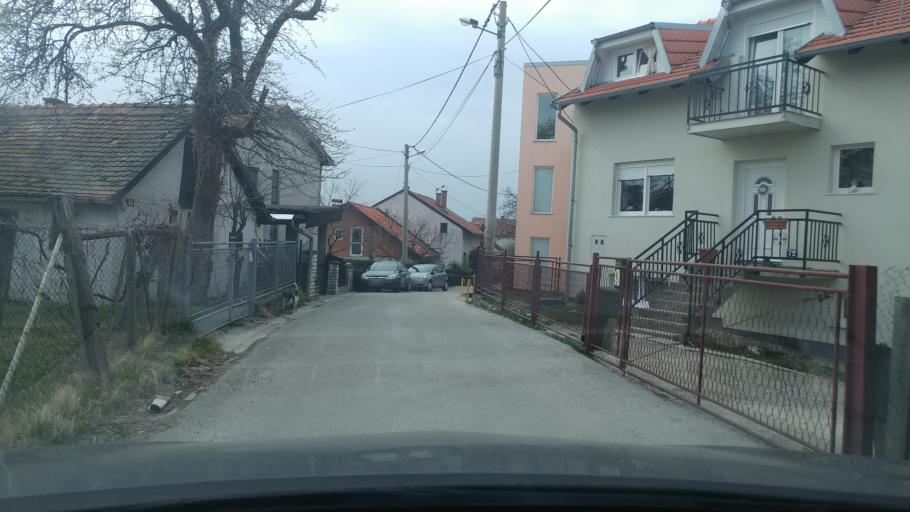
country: HR
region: Grad Zagreb
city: Stenjevec
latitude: 45.8493
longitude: 15.9256
